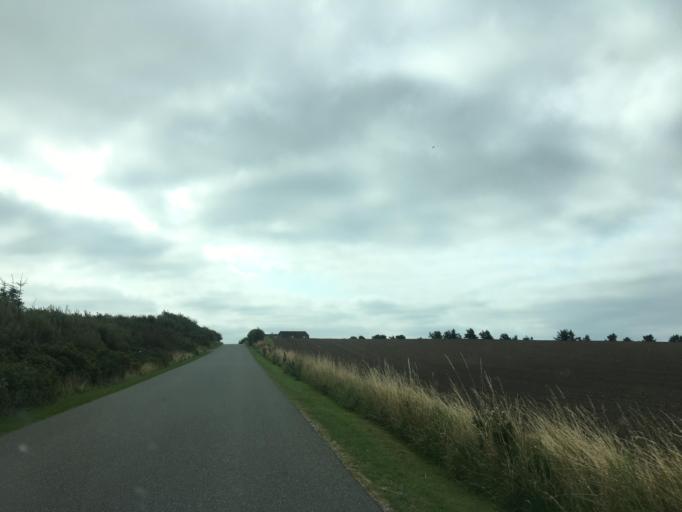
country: DK
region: Central Jutland
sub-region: Lemvig Kommune
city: Thyboron
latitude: 56.7868
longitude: 8.2842
